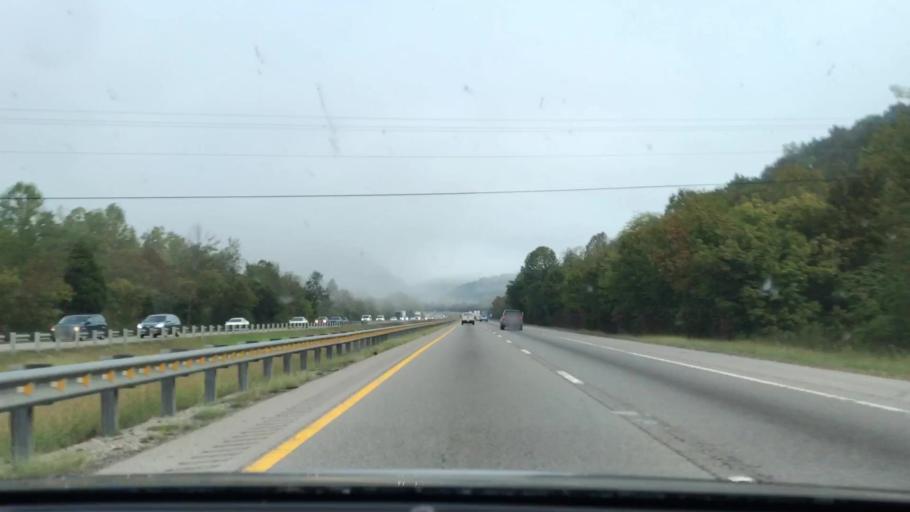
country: US
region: Tennessee
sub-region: Sumner County
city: Millersville
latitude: 36.3899
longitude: -86.7156
